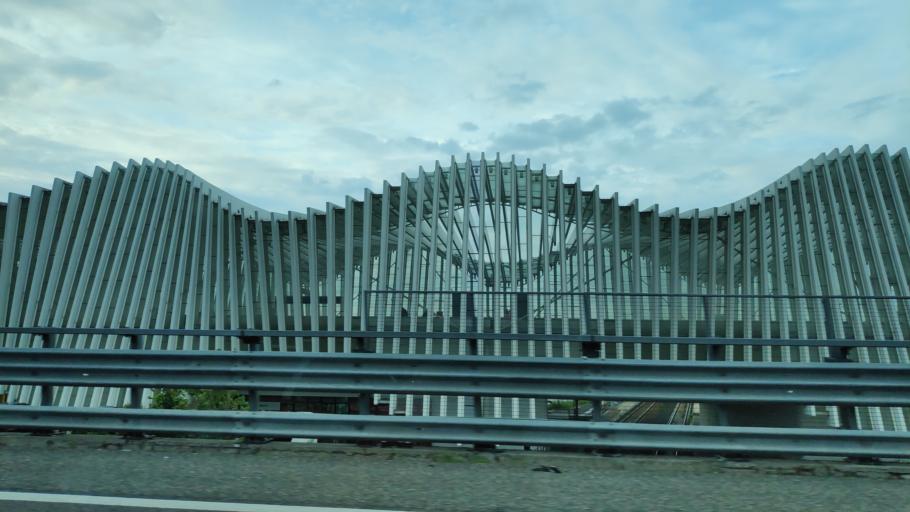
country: IT
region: Emilia-Romagna
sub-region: Provincia di Reggio Emilia
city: Reggio nell'Emilia
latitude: 44.7237
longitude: 10.6551
